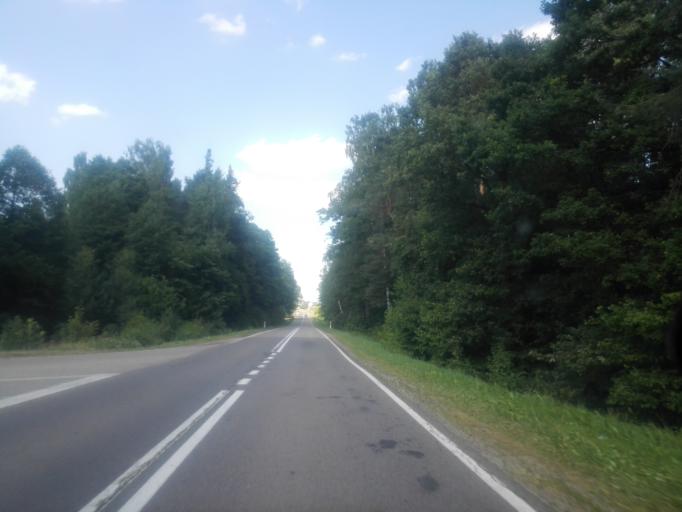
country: PL
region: Podlasie
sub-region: Powiat sejnenski
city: Sejny
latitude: 54.0336
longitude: 23.3537
